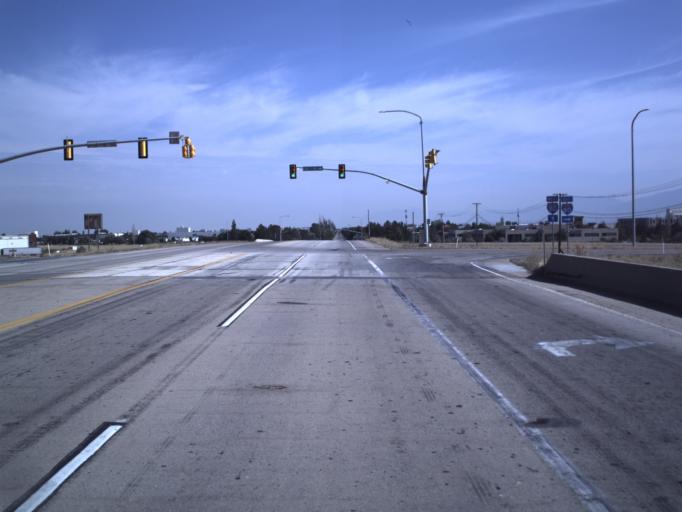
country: US
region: Utah
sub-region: Salt Lake County
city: West Valley City
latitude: 40.7685
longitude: -112.0250
